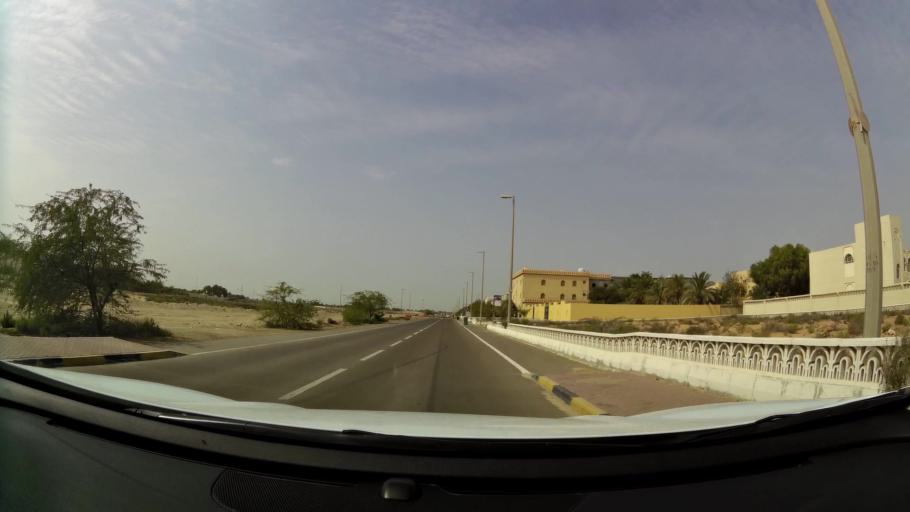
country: AE
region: Abu Dhabi
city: Abu Dhabi
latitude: 24.5407
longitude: 54.6674
